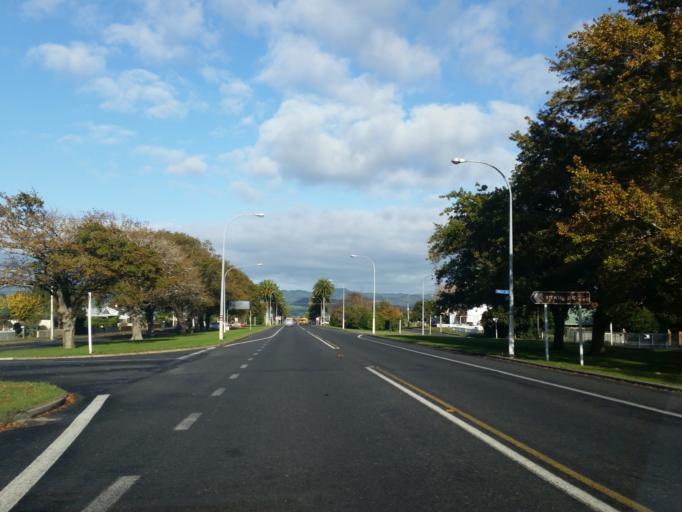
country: NZ
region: Waikato
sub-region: Hauraki District
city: Waihi
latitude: -37.3946
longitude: 175.8307
